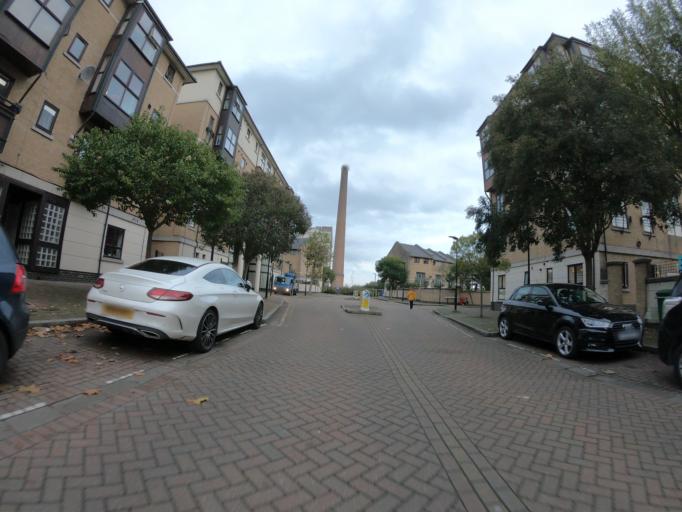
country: GB
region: England
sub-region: Greater London
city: East Ham
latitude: 51.5048
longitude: 0.0268
